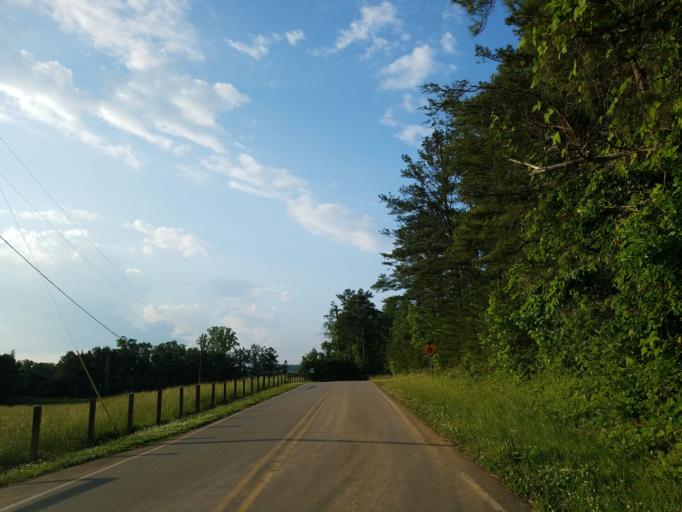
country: US
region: Georgia
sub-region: Cherokee County
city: Ball Ground
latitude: 34.3165
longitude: -84.3873
